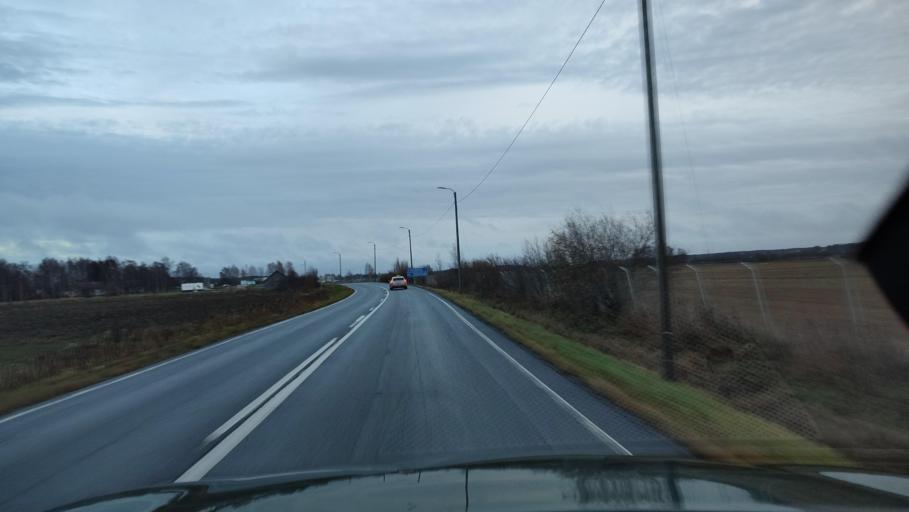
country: FI
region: Ostrobothnia
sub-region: Vaasa
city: Ristinummi
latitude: 63.0448
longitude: 21.7492
